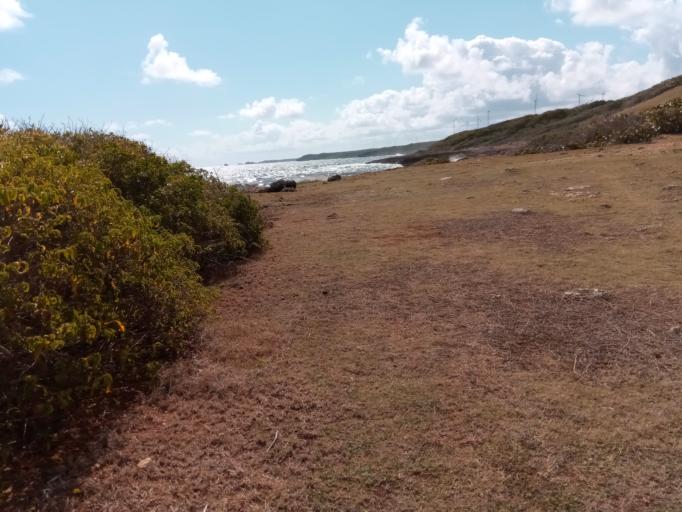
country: GP
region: Guadeloupe
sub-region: Guadeloupe
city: Saint-Francois
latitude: 16.2772
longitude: -61.2460
